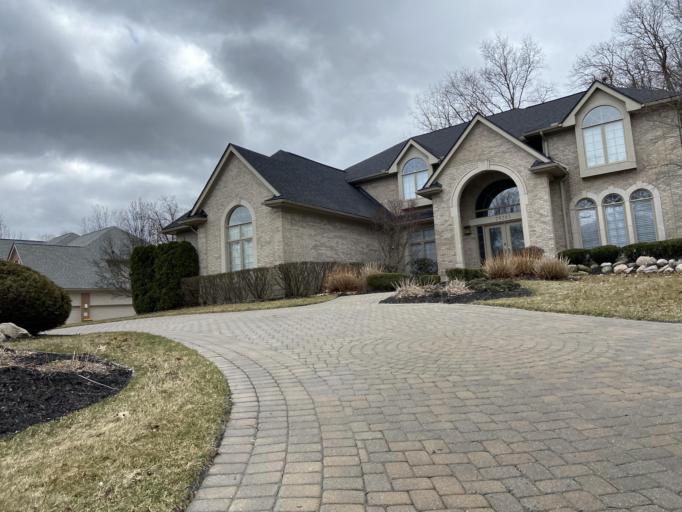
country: US
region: Michigan
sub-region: Oakland County
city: Franklin
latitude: 42.5024
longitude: -83.3238
